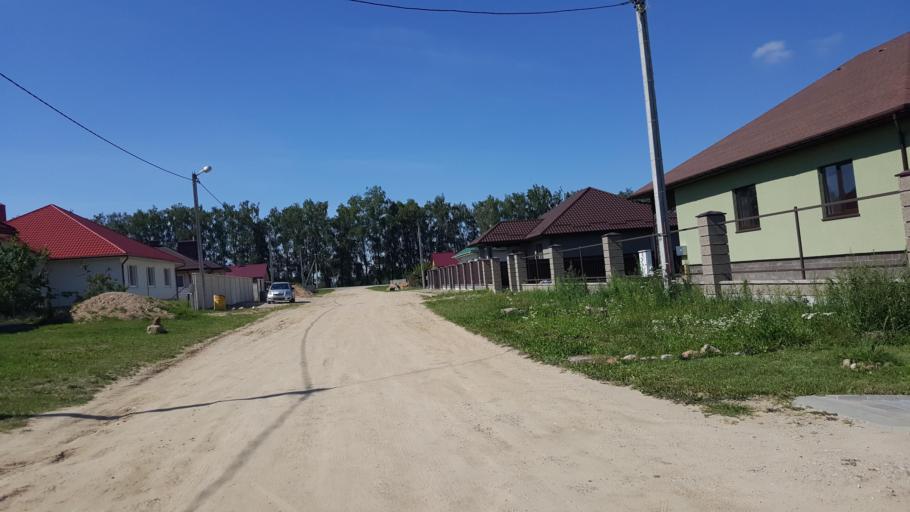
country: BY
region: Brest
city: Charnawchytsy
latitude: 52.2580
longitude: 23.5880
